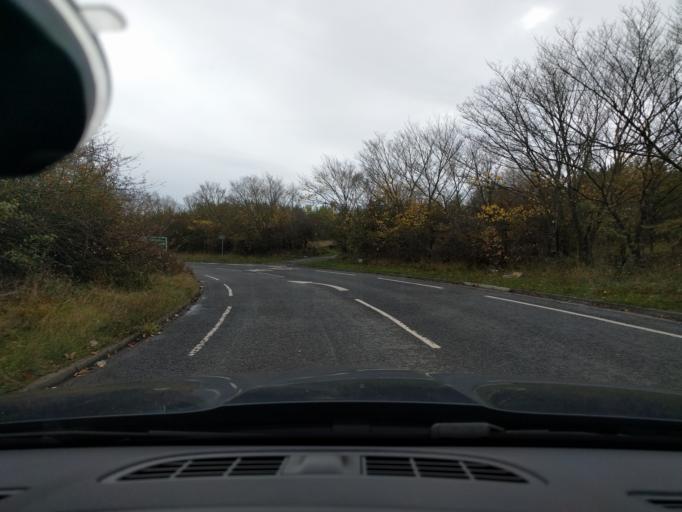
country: GB
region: England
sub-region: Northumberland
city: Ashington
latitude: 55.1482
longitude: -1.5528
